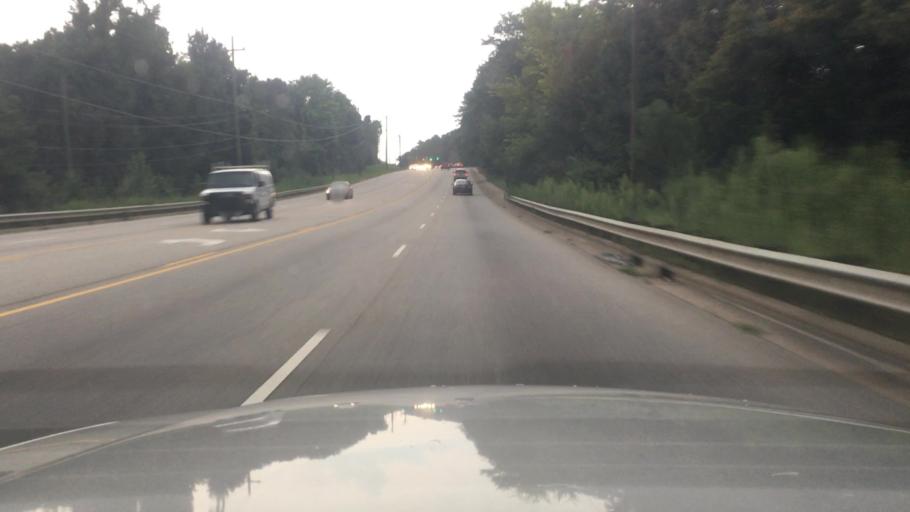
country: US
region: North Carolina
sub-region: Cumberland County
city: Fort Bragg
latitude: 35.0735
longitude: -79.0114
